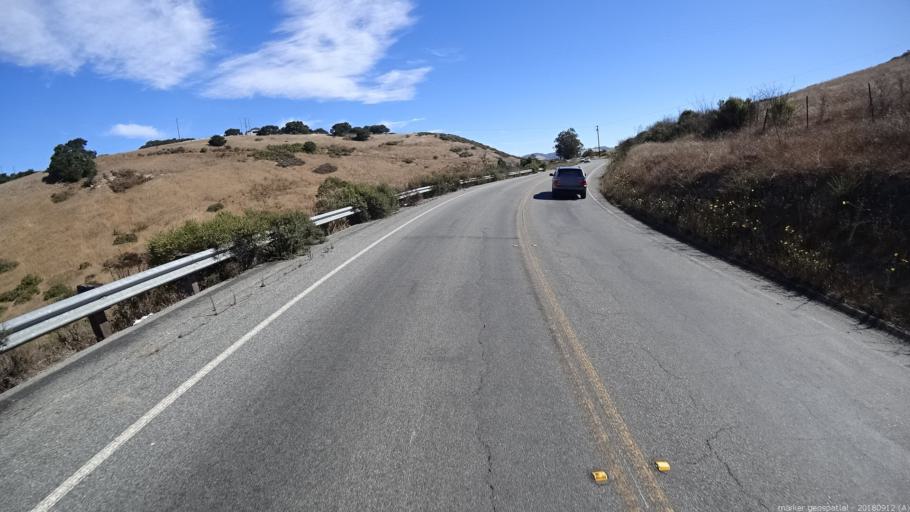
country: US
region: California
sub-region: Monterey County
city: Carmel Valley Village
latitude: 36.5297
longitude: -121.7518
